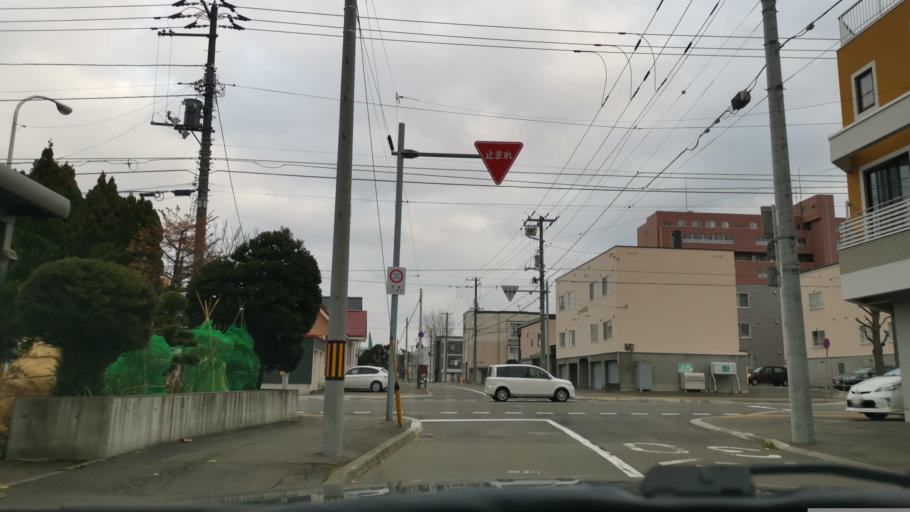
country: JP
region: Hokkaido
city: Sapporo
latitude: 43.0453
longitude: 141.4048
